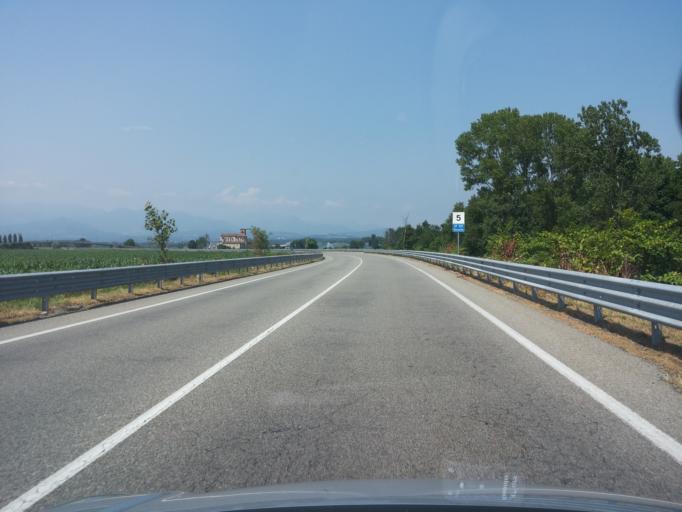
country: IT
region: Piedmont
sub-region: Provincia di Biella
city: Mottalciata
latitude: 45.5123
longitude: 8.2118
